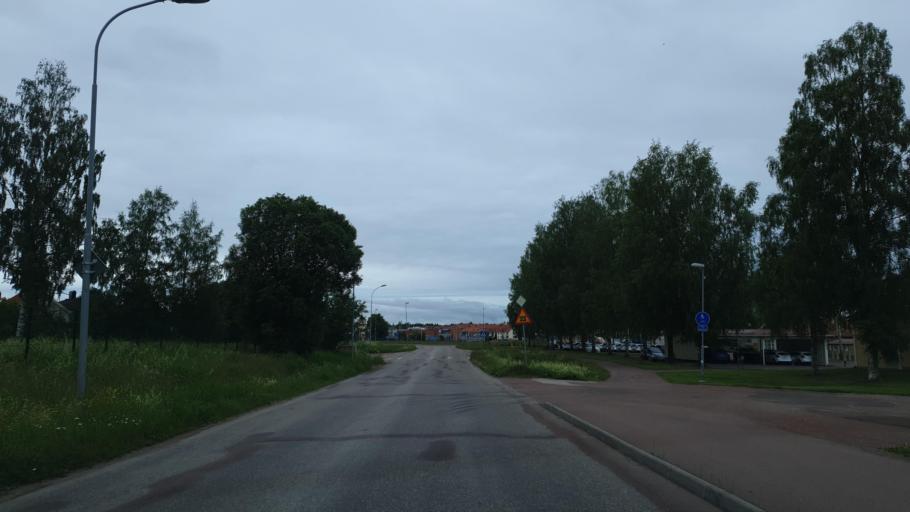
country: SE
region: Dalarna
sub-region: Mora Kommun
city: Mora
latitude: 60.9986
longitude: 14.5420
